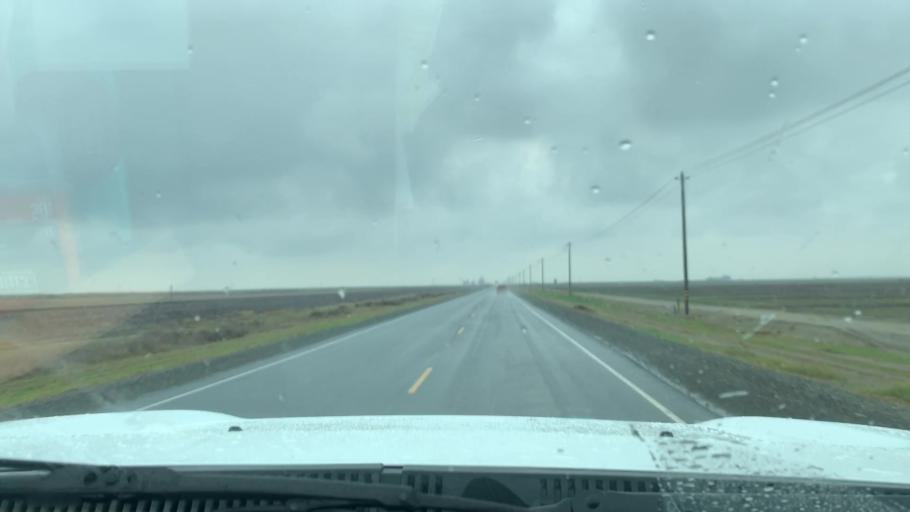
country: US
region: California
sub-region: Tulare County
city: Alpaugh
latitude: 35.9657
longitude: -119.4596
